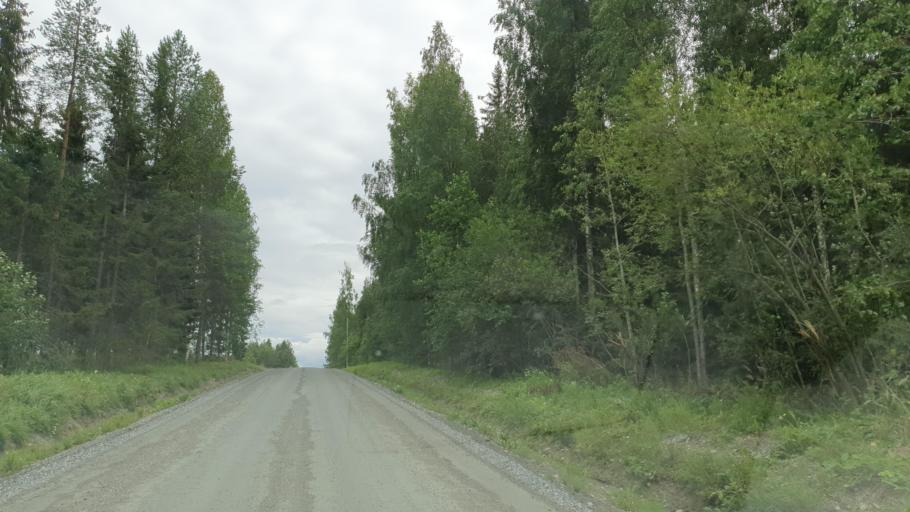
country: FI
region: Northern Savo
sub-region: Ylae-Savo
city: Iisalmi
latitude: 63.5254
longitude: 27.0911
